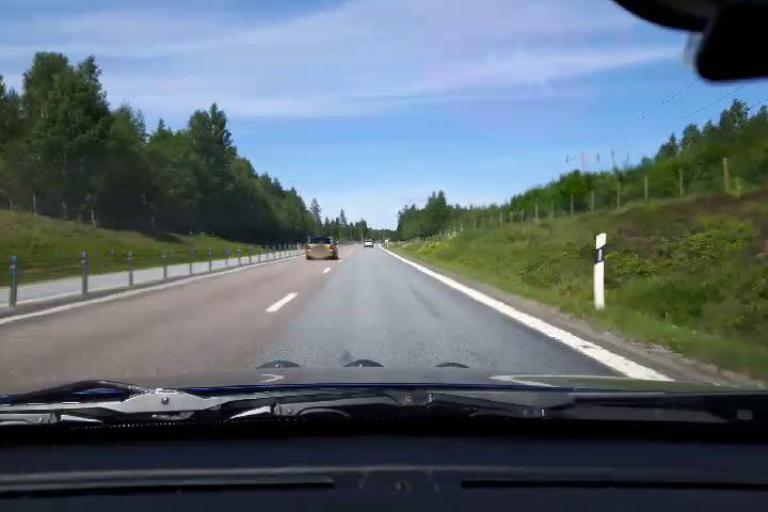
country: SE
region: Gaevleborg
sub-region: Gavle Kommun
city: Norrsundet
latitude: 60.9346
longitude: 17.0133
